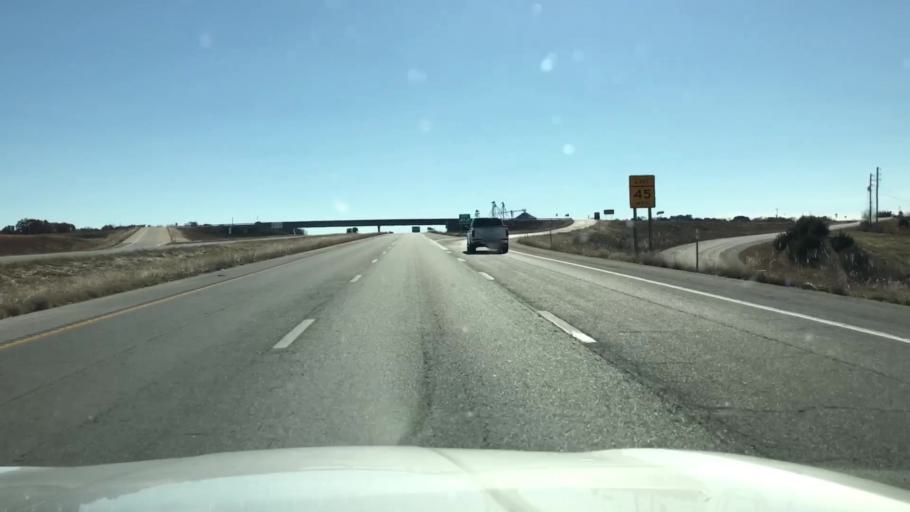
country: US
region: Missouri
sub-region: Jasper County
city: Carthage
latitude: 37.1001
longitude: -94.3115
